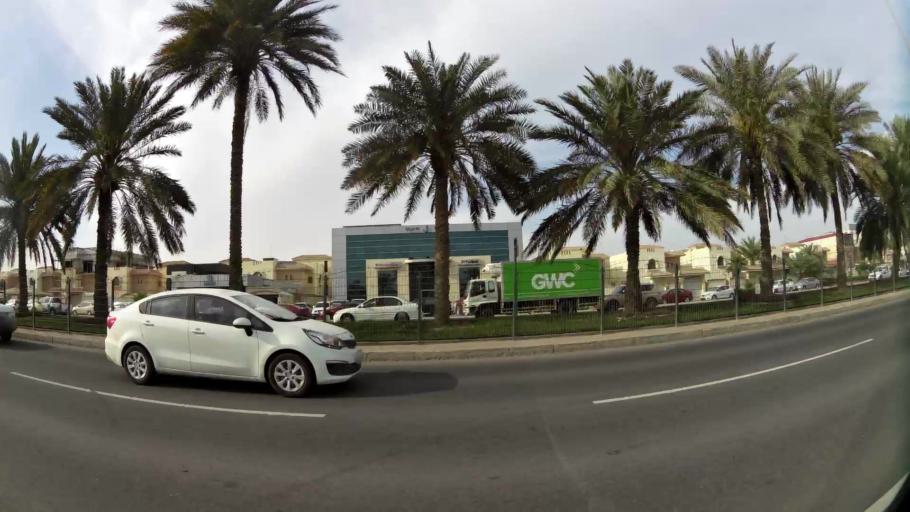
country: QA
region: Baladiyat ad Dawhah
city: Doha
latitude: 25.2543
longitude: 51.5294
